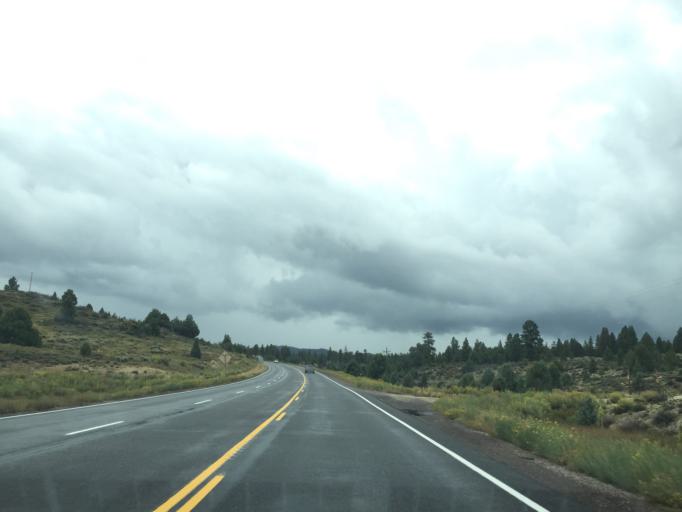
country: US
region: Utah
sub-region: Garfield County
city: Panguitch
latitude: 37.4834
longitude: -112.5144
